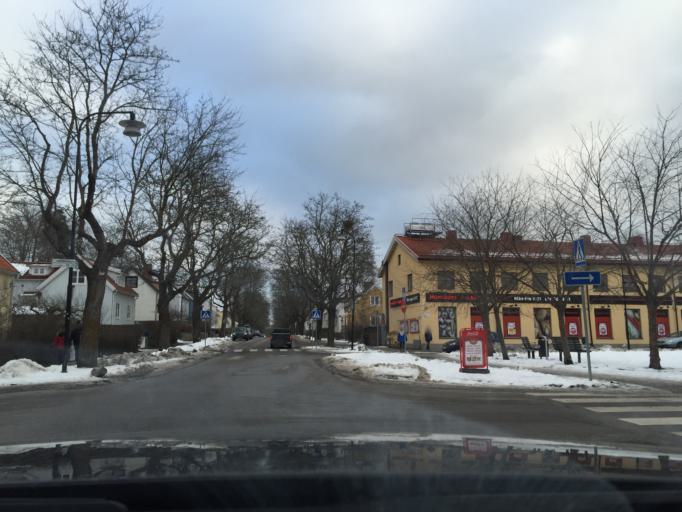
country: SE
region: Stockholm
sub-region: Stockholms Kommun
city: Bromma
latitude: 59.3474
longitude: 17.9080
